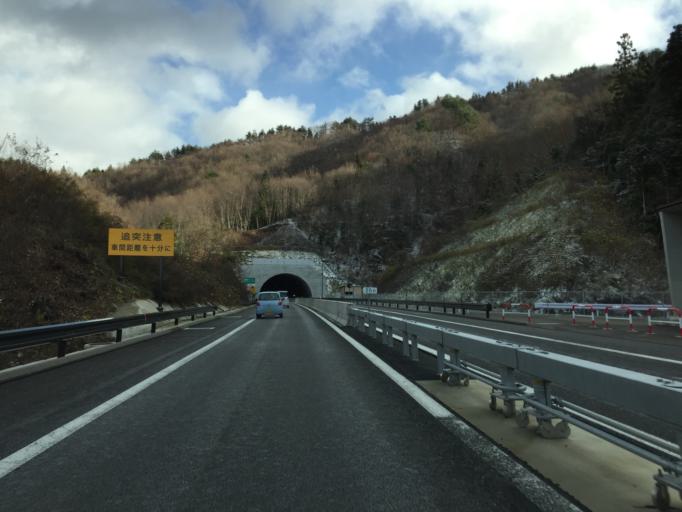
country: JP
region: Fukushima
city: Yanagawamachi-saiwaicho
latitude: 37.7532
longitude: 140.6613
